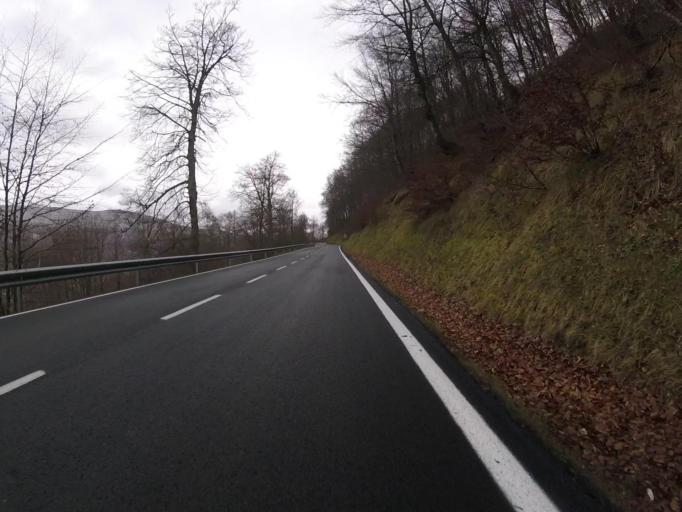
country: ES
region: Navarre
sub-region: Provincia de Navarra
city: Arbizu
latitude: 42.8637
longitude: -2.0203
